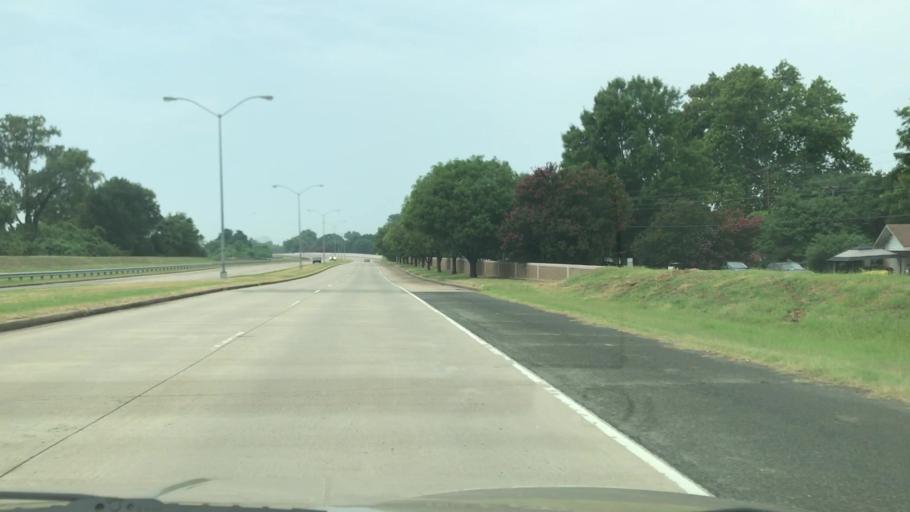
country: US
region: Louisiana
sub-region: Bossier Parish
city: Bossier City
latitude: 32.5070
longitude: -93.7127
